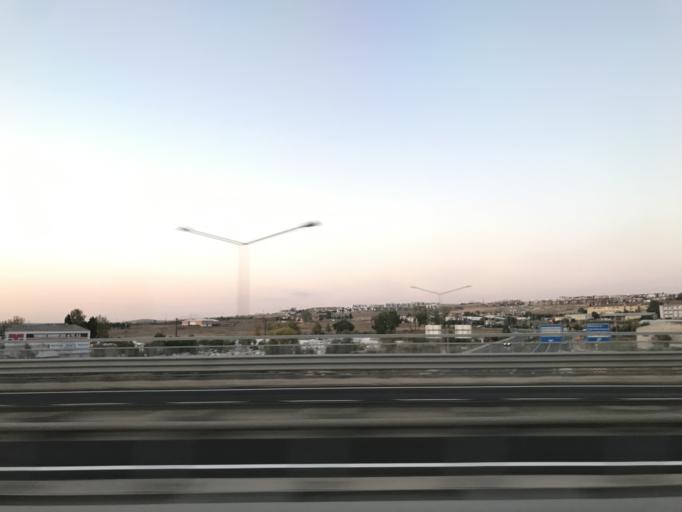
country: TR
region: Tekirdag
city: Tekirdag
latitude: 40.9896
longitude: 27.5747
